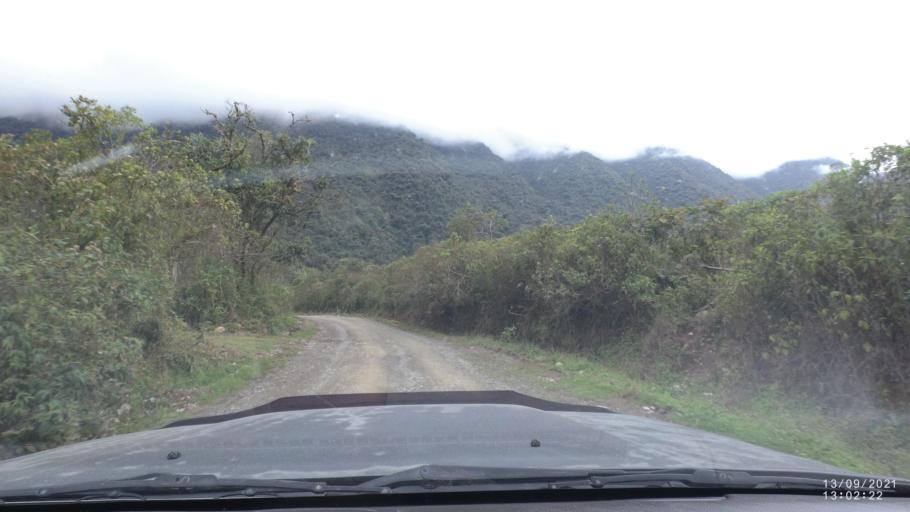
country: BO
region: Cochabamba
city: Colomi
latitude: -17.2298
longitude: -65.8185
